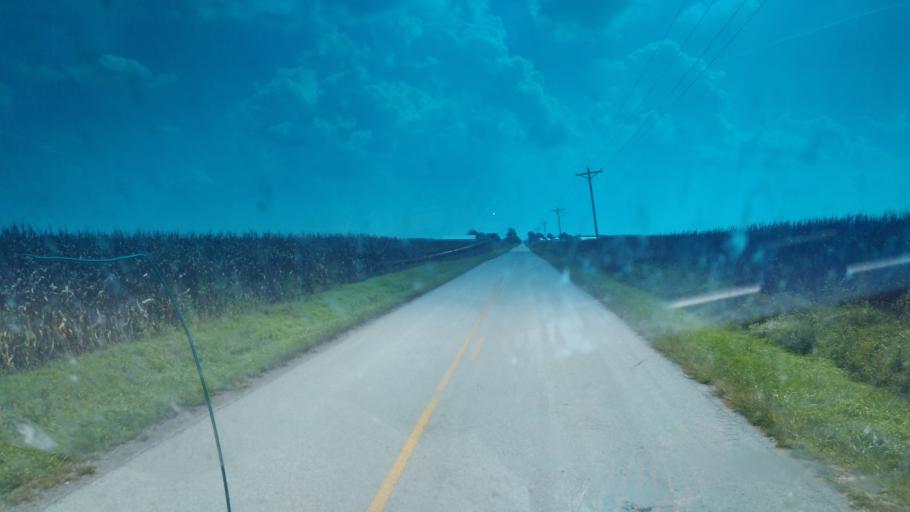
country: US
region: Ohio
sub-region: Hardin County
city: Kenton
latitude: 40.6737
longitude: -83.7287
